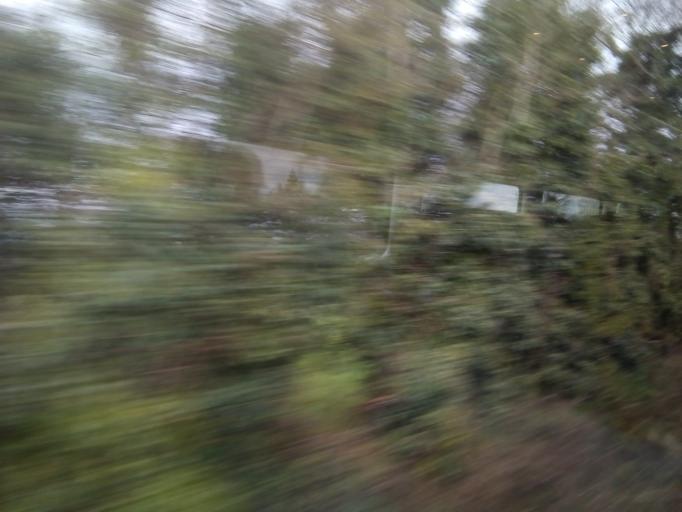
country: IE
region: Leinster
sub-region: An Longfort
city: Edgeworthstown
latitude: 53.6854
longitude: -7.5833
